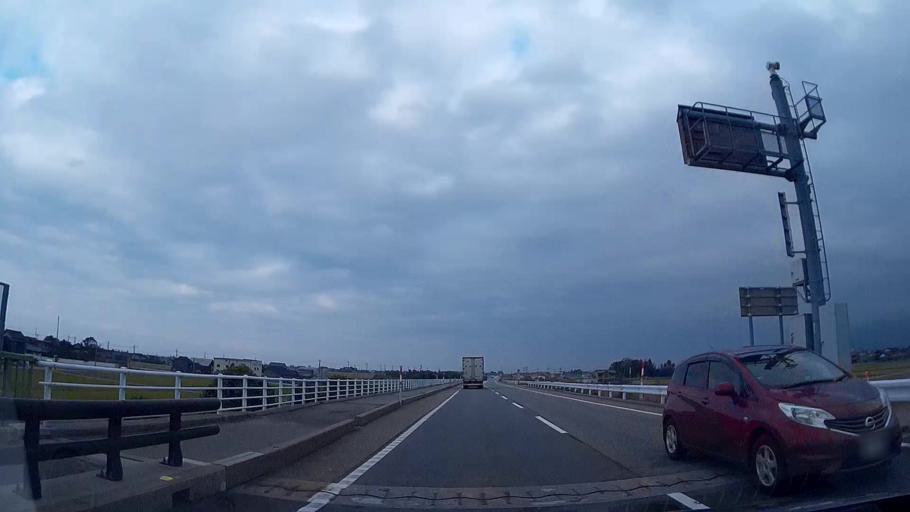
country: JP
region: Toyama
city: Nyuzen
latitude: 36.9096
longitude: 137.4549
